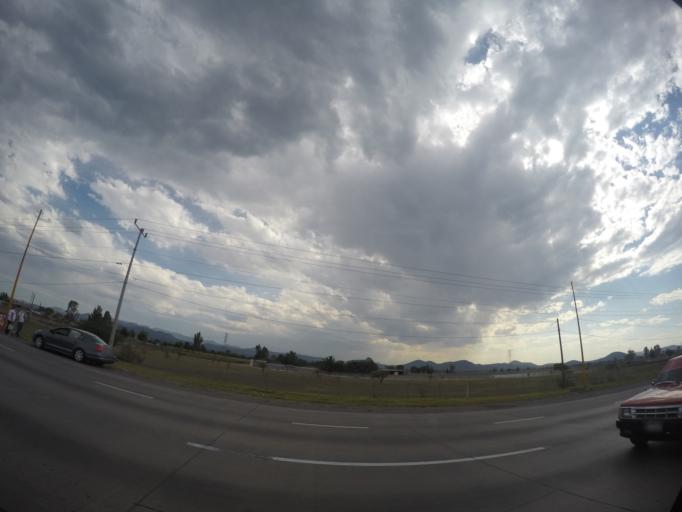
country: MX
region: Queretaro
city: La Estancia
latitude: 20.4118
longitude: -100.0395
